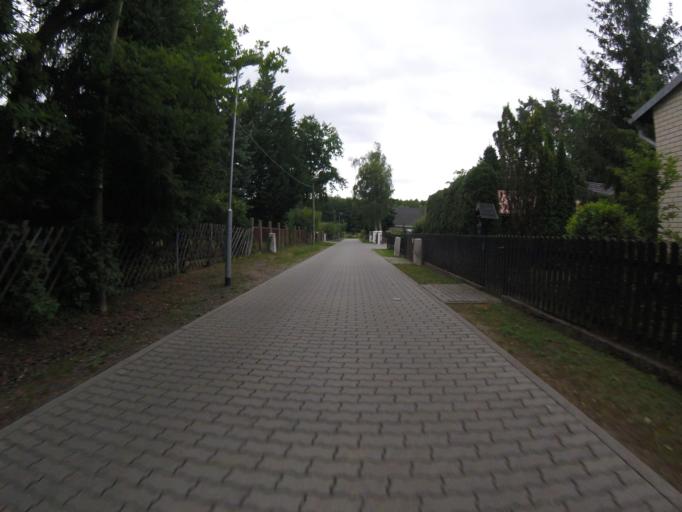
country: DE
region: Brandenburg
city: Bestensee
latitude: 52.2237
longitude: 13.6356
